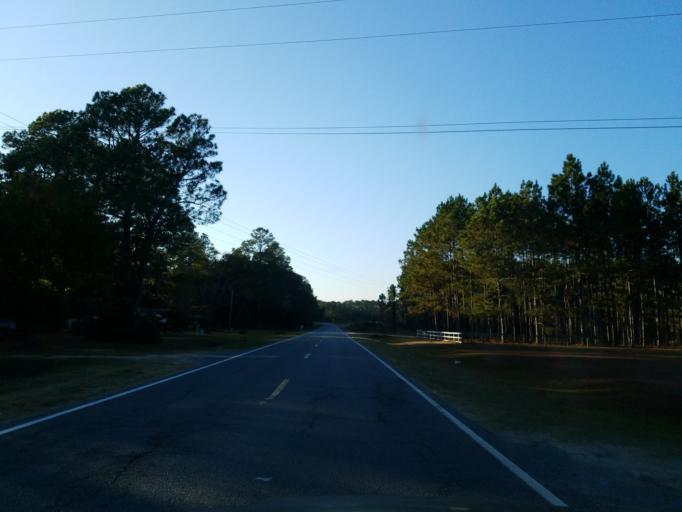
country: US
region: Georgia
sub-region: Berrien County
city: Nashville
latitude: 31.1930
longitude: -83.2111
